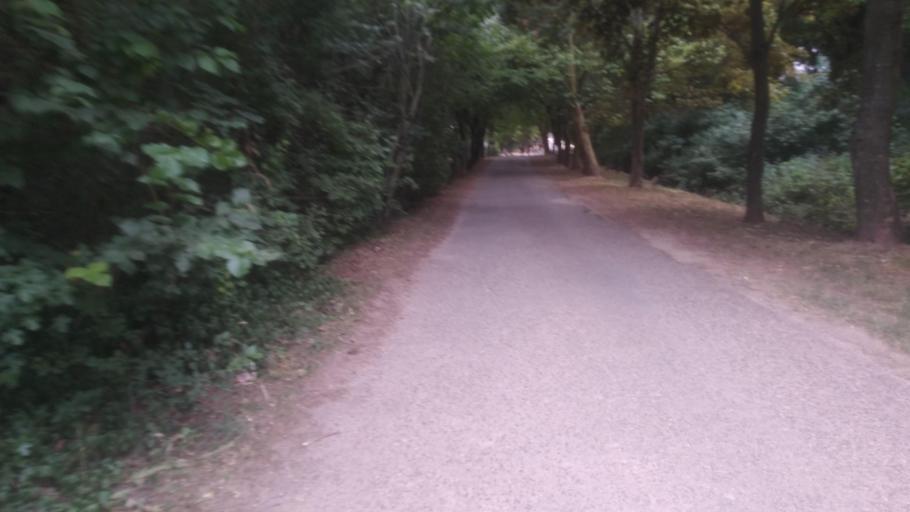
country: HU
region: Veszprem
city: Szentkiralyszabadja
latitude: 46.9988
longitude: 17.9738
